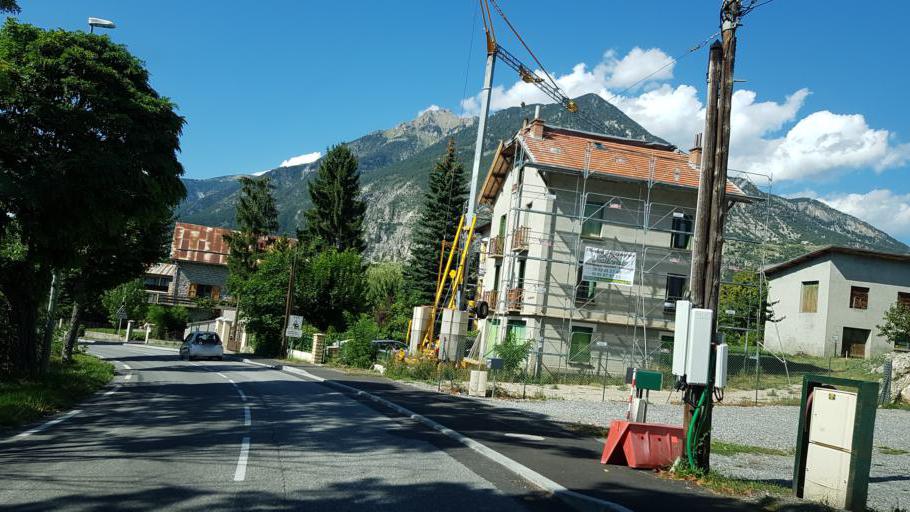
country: FR
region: Provence-Alpes-Cote d'Azur
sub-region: Departement des Hautes-Alpes
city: Guillestre
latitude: 44.6590
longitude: 6.6542
